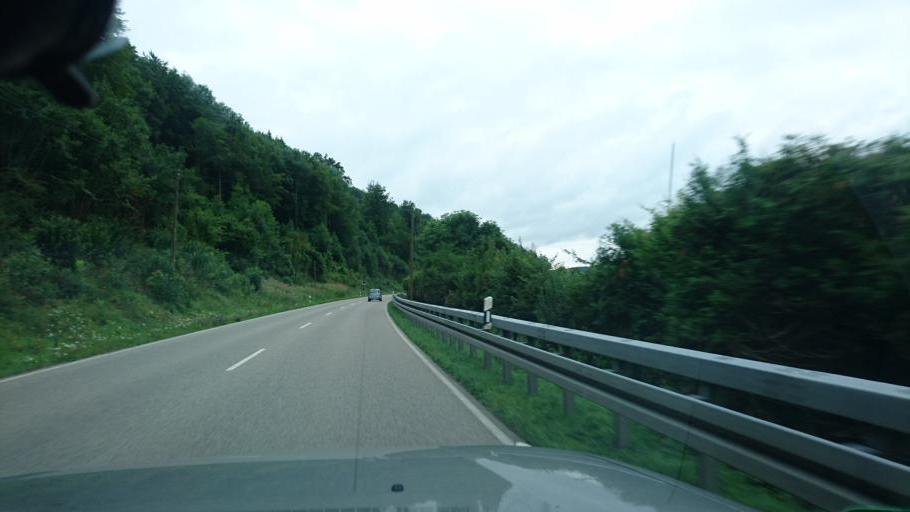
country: DE
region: Baden-Wuerttemberg
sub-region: Freiburg Region
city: Sulz am Neckar
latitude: 48.3524
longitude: 8.5924
